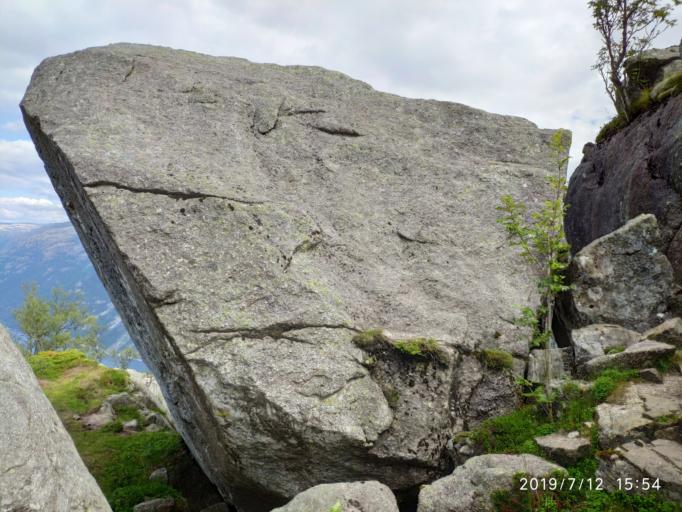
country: NO
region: Rogaland
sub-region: Forsand
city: Forsand
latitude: 58.9863
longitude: 6.1860
